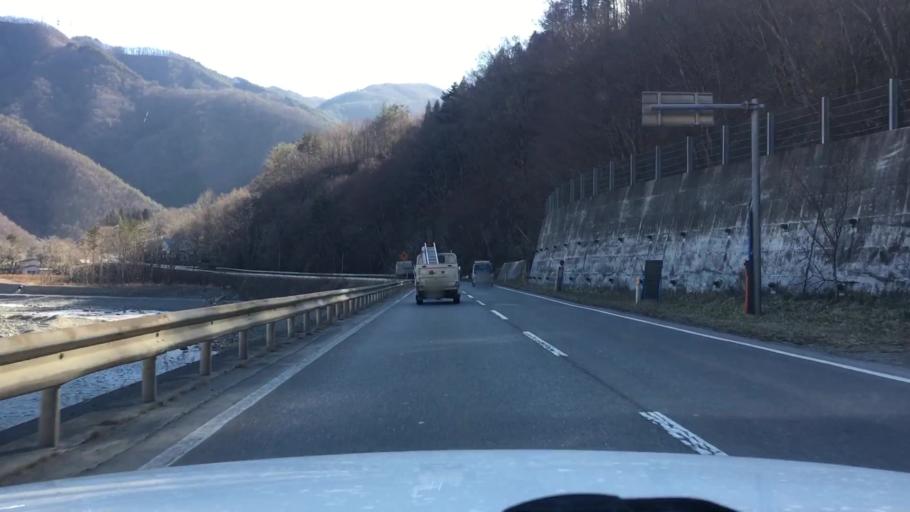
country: JP
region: Iwate
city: Miyako
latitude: 39.6261
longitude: 141.8090
